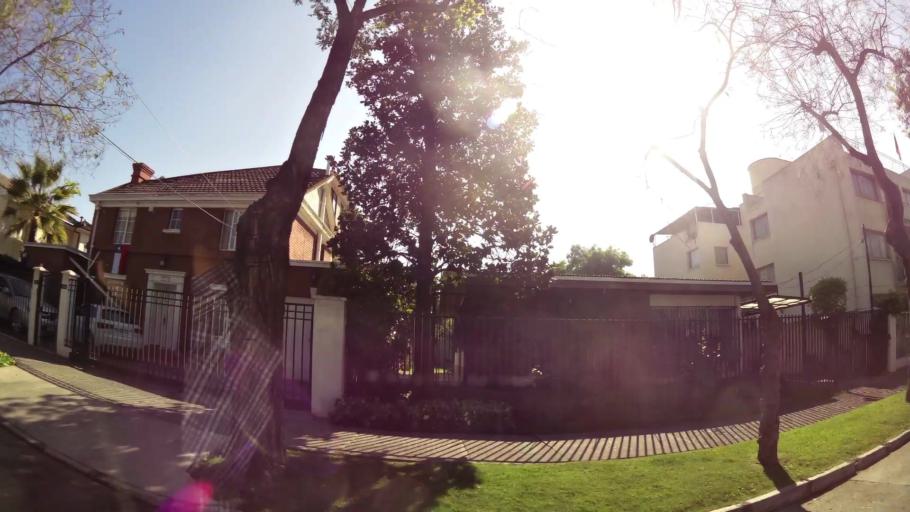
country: CL
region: Santiago Metropolitan
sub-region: Provincia de Santiago
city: Villa Presidente Frei, Nunoa, Santiago, Chile
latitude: -33.4371
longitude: -70.5872
